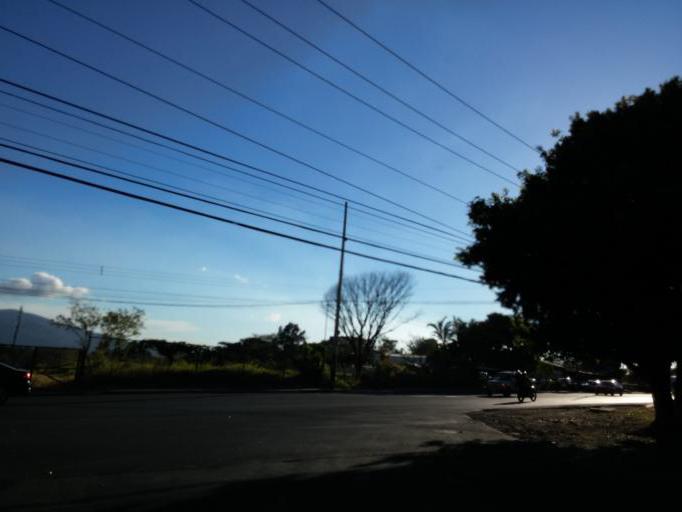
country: CR
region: Heredia
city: Llorente
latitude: 10.0071
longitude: -84.1765
